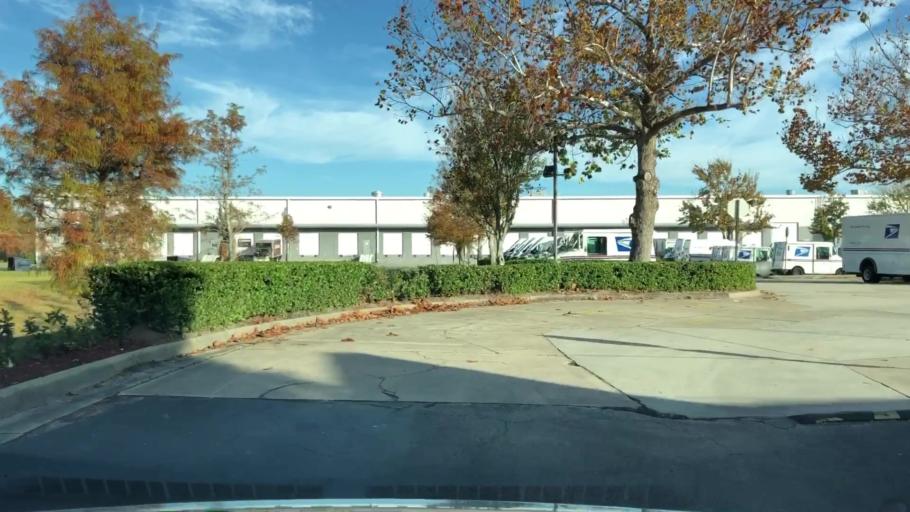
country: US
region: Florida
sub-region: Orange County
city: Conway
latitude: 28.4599
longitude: -81.2981
